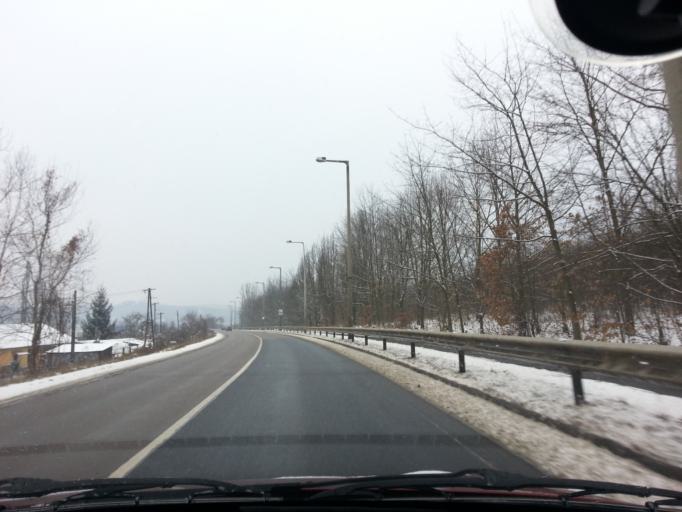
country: HU
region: Nograd
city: Salgotarjan
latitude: 48.0834
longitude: 19.7864
